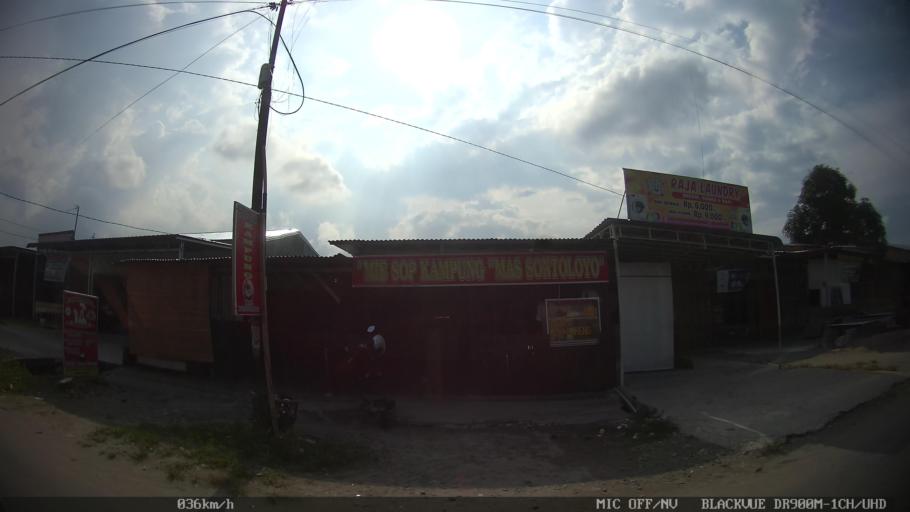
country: ID
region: North Sumatra
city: Medan
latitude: 3.5774
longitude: 98.7566
